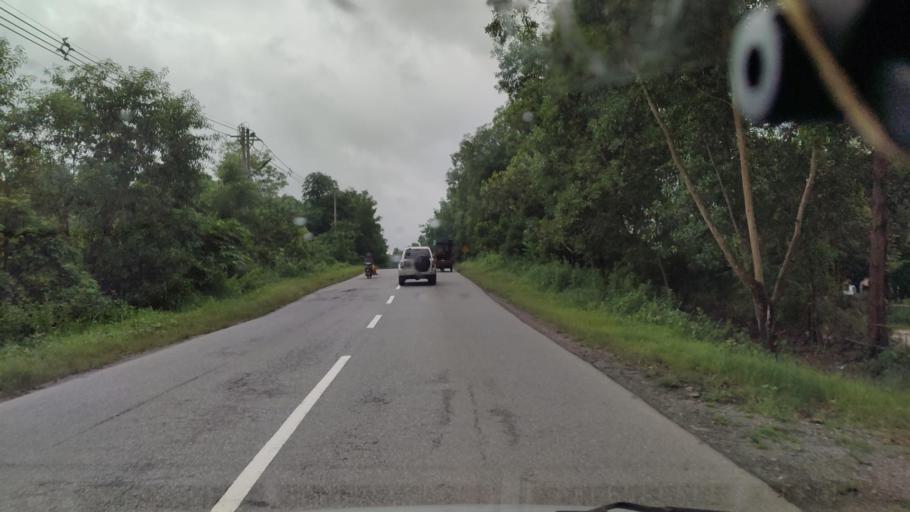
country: MM
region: Bago
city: Bago
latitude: 17.3308
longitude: 96.4427
